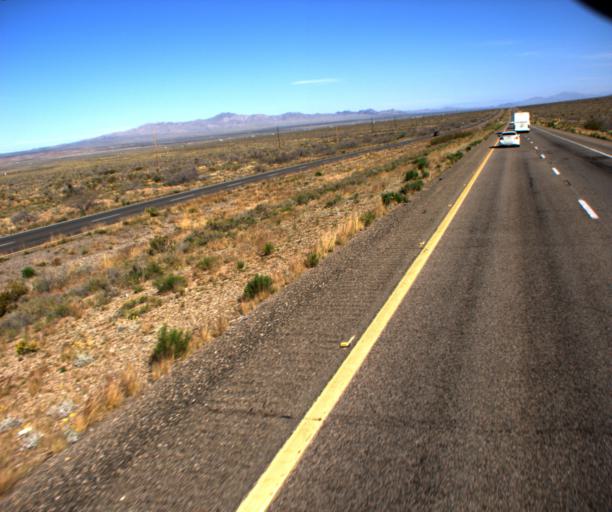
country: US
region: Arizona
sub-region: Mohave County
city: Dolan Springs
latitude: 35.4520
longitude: -114.2986
